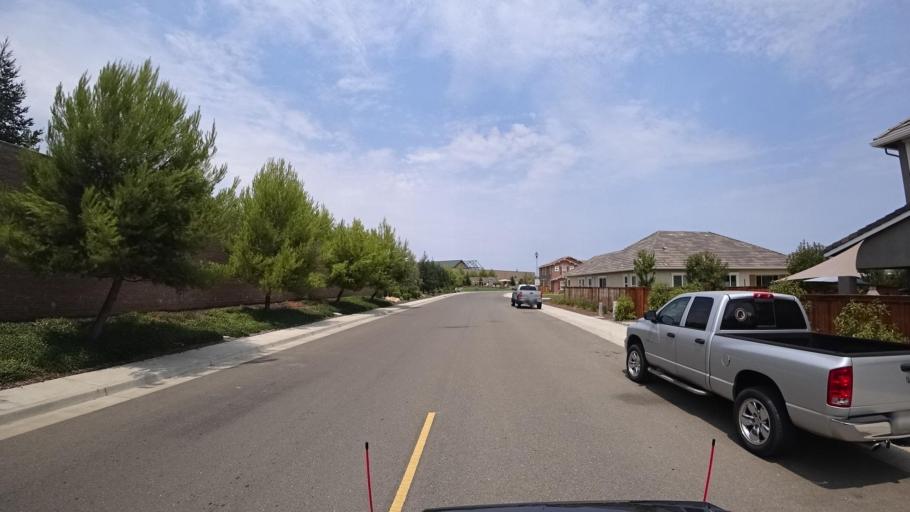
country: US
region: California
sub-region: Placer County
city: Loomis
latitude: 38.8024
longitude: -121.2008
